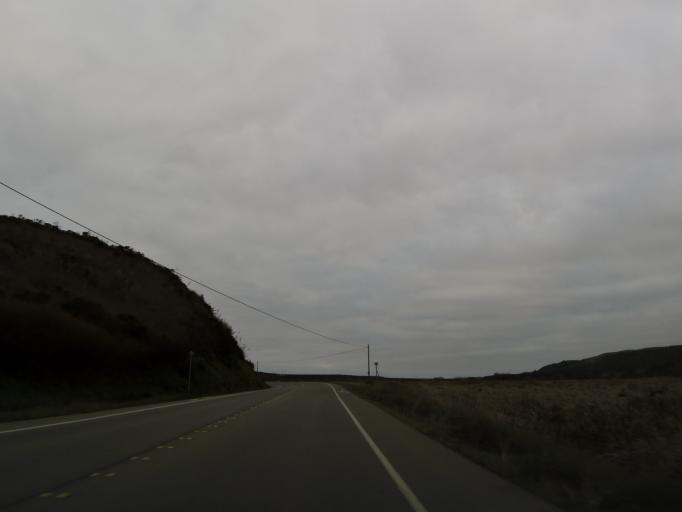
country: US
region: California
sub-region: San Mateo County
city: Portola Valley
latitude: 37.2512
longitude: -122.4020
